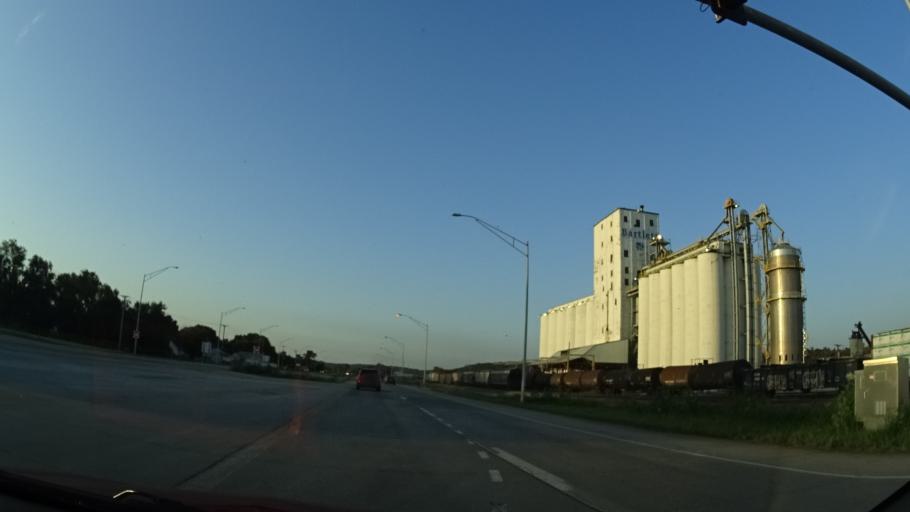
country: US
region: Iowa
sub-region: Pottawattamie County
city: Council Bluffs
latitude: 41.2343
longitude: -95.8513
